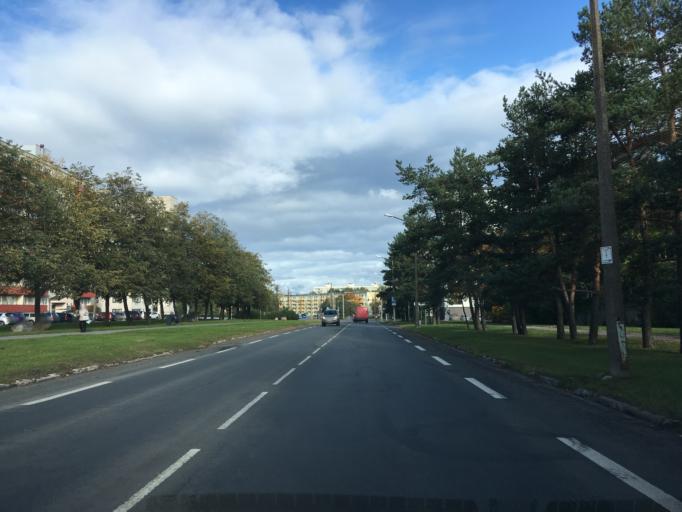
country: EE
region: Harju
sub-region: Tallinna linn
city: Tallinn
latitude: 59.3970
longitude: 24.6821
